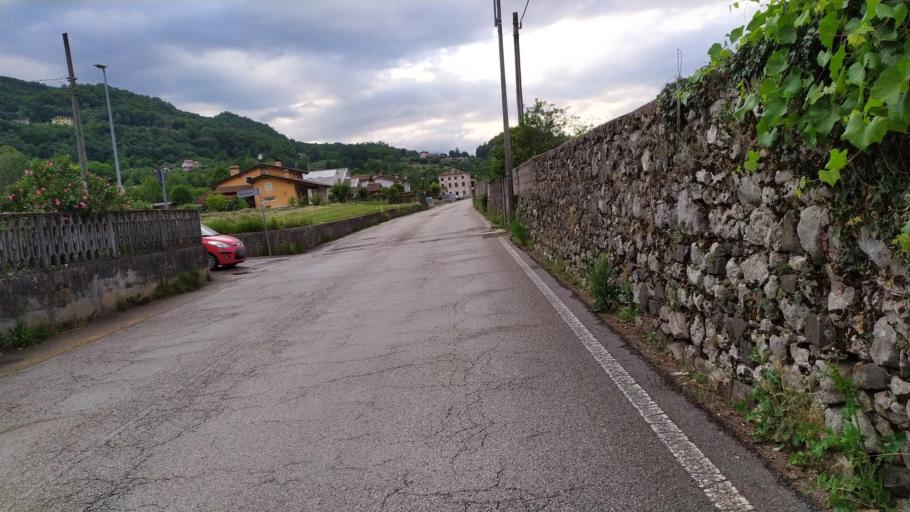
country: IT
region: Veneto
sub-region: Provincia di Vicenza
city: Isola Vicentina
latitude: 45.6350
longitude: 11.4234
